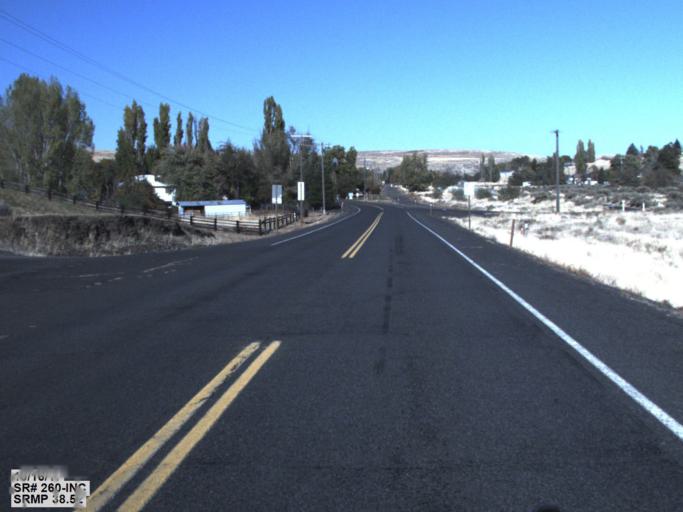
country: US
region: Washington
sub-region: Adams County
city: Ritzville
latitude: 46.7466
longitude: -118.3190
